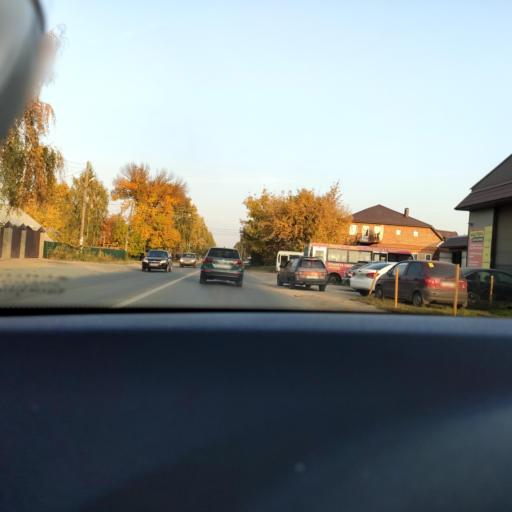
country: RU
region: Samara
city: Petra-Dubrava
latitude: 53.2530
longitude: 50.3225
